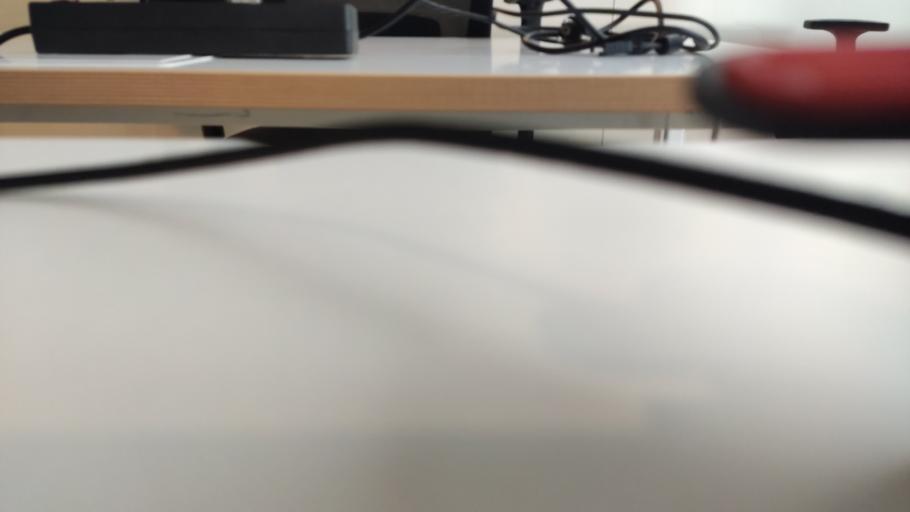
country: RU
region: Moskovskaya
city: Rogachevo
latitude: 56.4274
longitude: 37.1039
